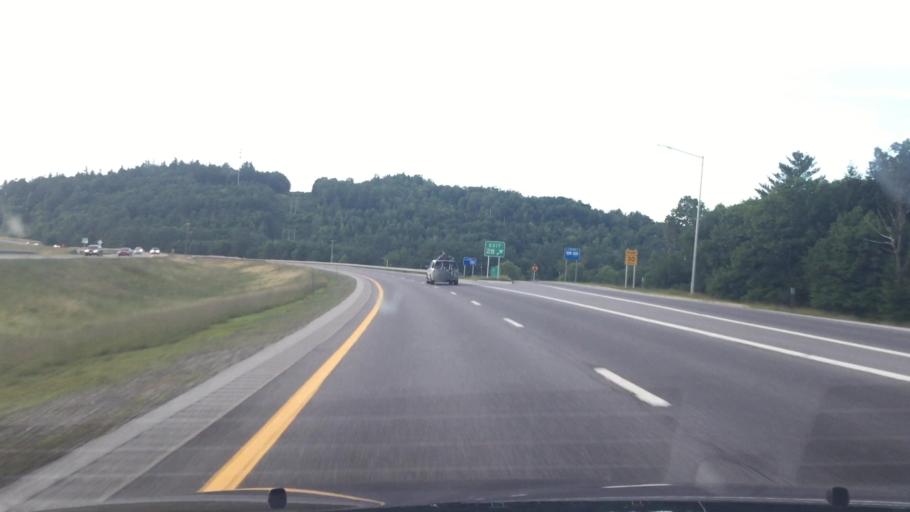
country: US
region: New Hampshire
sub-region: Grafton County
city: Thornton
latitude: 43.8472
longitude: -71.6452
